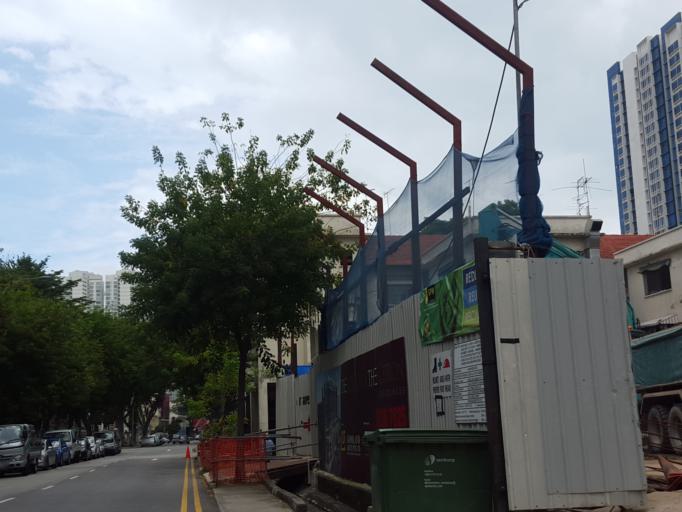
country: SG
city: Singapore
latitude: 1.3130
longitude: 103.8573
